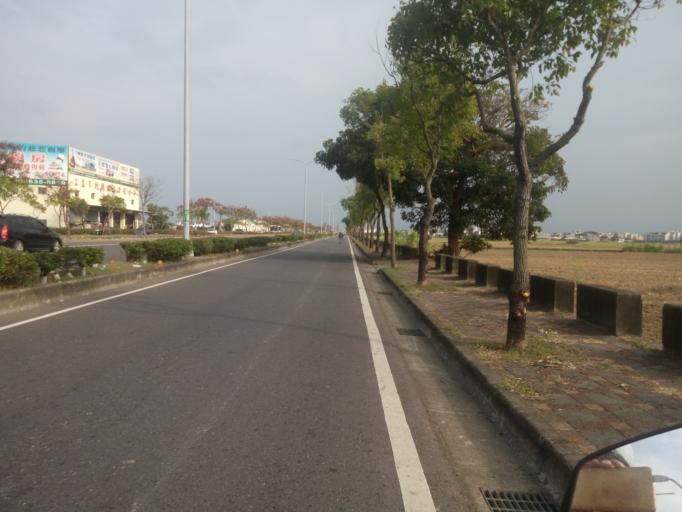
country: TW
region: Taiwan
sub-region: Chiayi
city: Jiayi Shi
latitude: 23.4870
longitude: 120.4028
